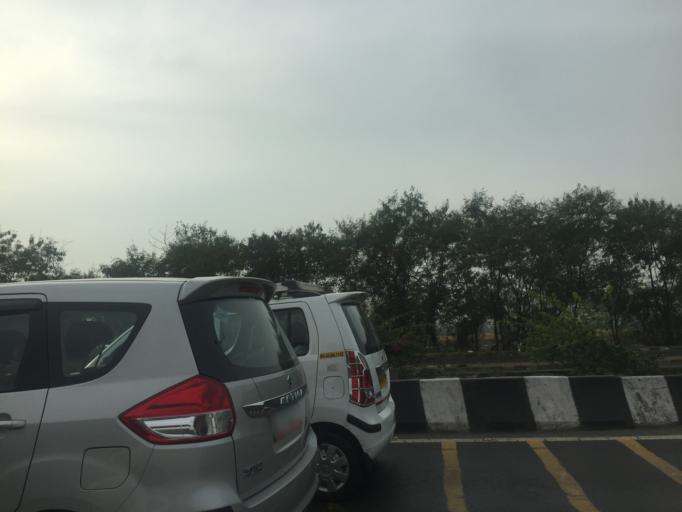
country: IN
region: Maharashtra
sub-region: Mumbai Suburban
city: Powai
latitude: 19.1394
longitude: 72.9474
